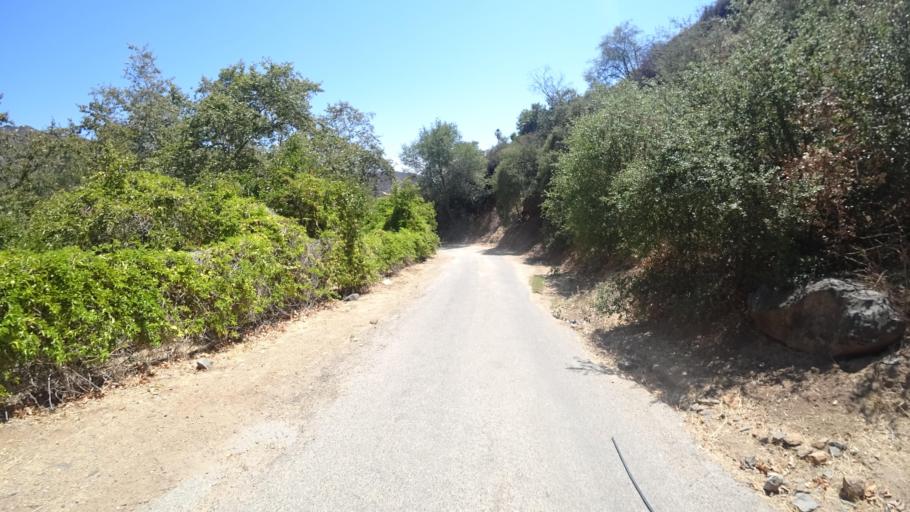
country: US
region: California
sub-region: San Diego County
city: Rainbow
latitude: 33.3837
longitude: -117.1124
